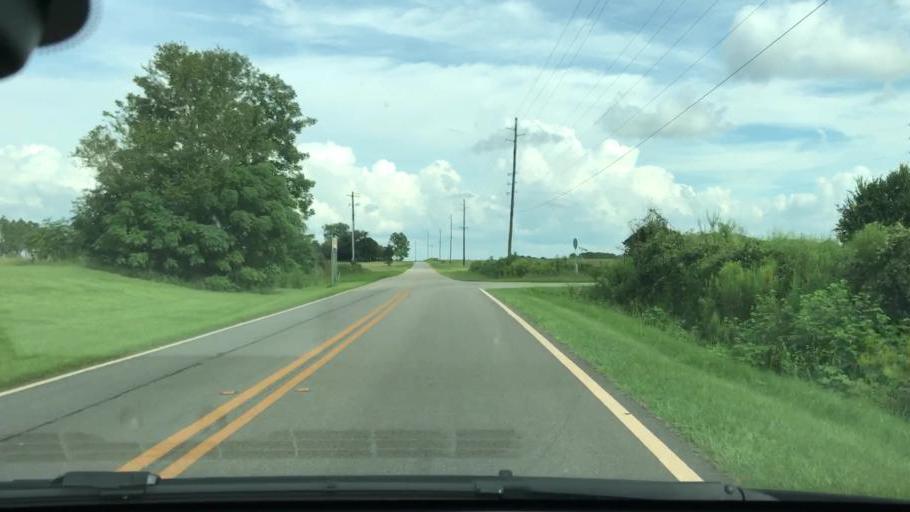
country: US
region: Georgia
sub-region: Clay County
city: Fort Gaines
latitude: 31.5304
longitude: -84.9551
